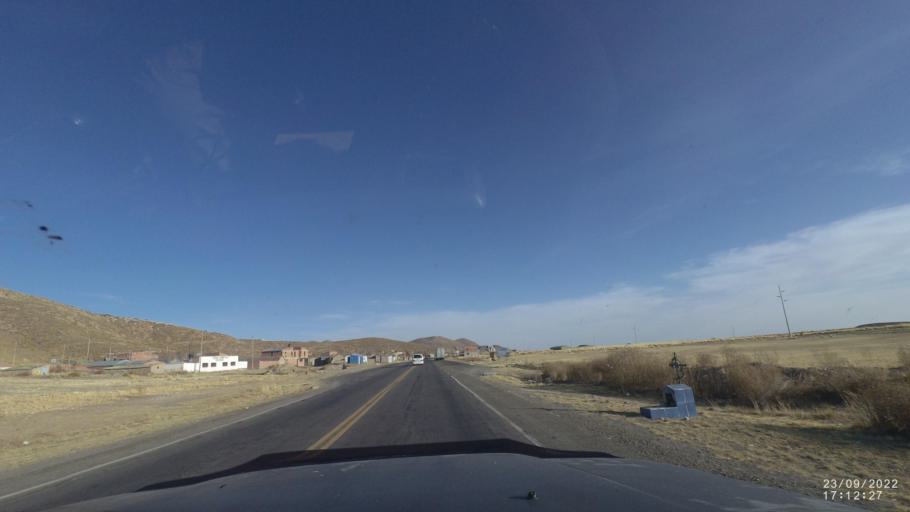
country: BO
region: Oruro
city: Totoral
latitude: -18.7040
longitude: -66.8772
